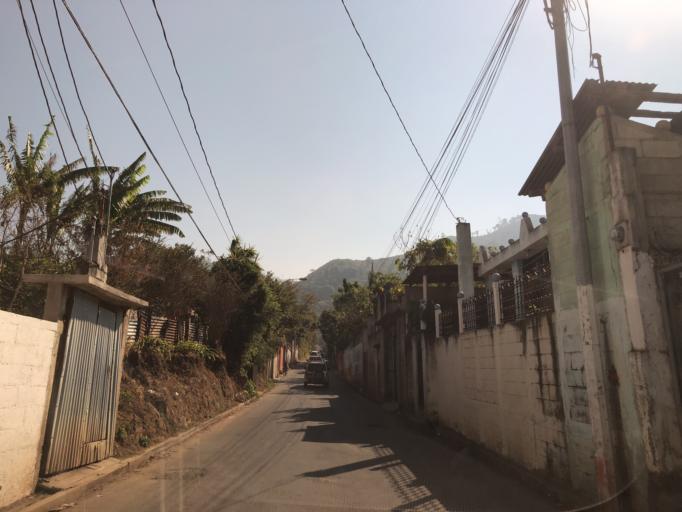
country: GT
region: Guatemala
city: Santa Catarina Pinula
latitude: 14.5398
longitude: -90.5093
